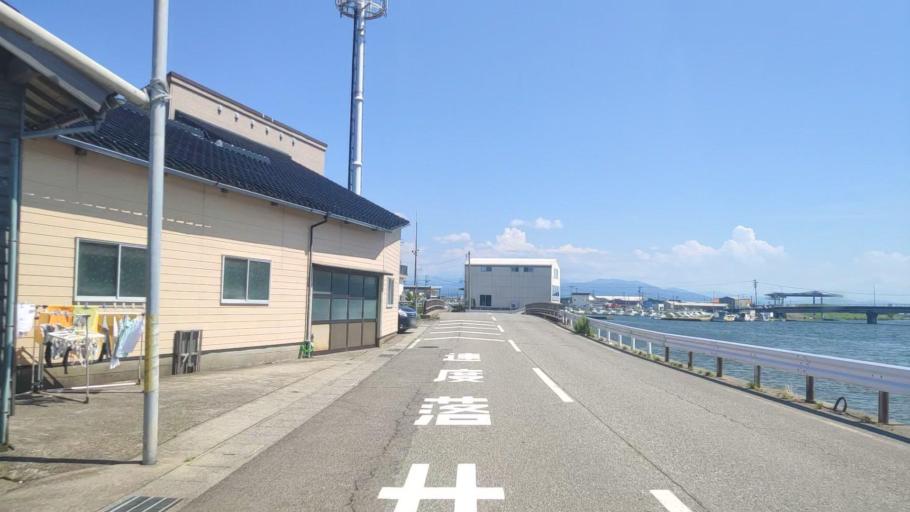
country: JP
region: Ishikawa
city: Kanazawa-shi
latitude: 36.5995
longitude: 136.5895
